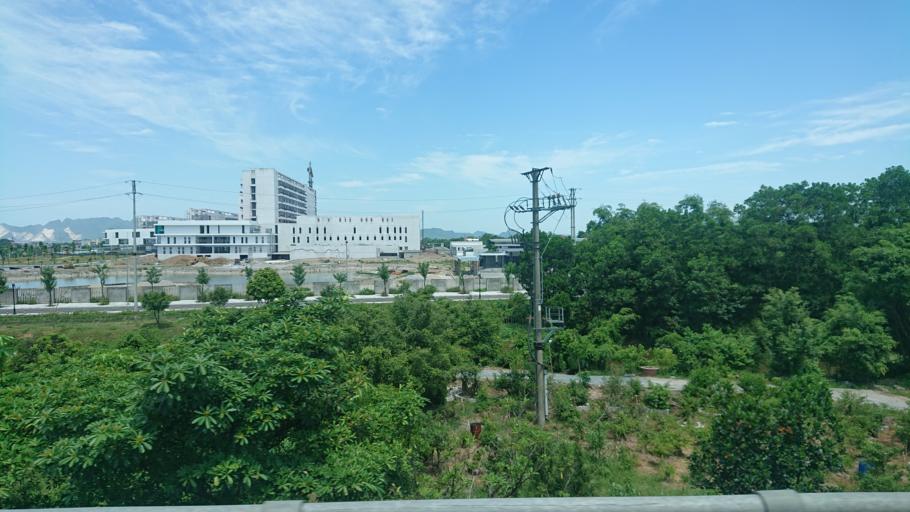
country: VN
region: Ha Nam
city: Thanh Pho Phu Ly
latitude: 20.5420
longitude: 105.9476
